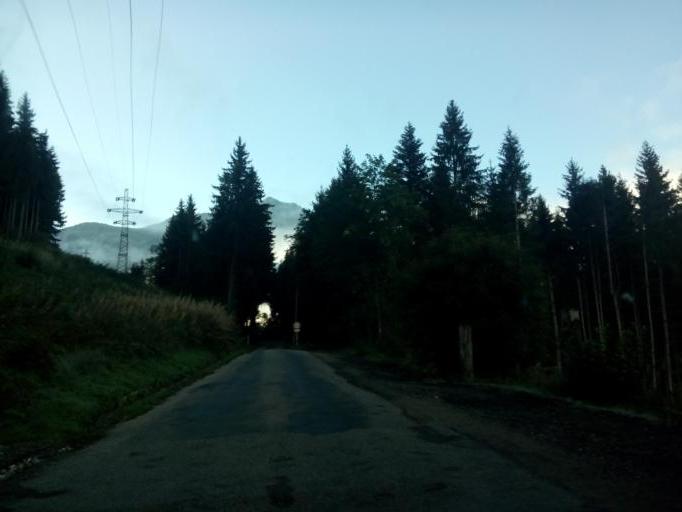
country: FR
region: Rhone-Alpes
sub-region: Departement de l'Isere
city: Le Champ-pres-Froges
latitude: 45.2450
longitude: 5.9787
